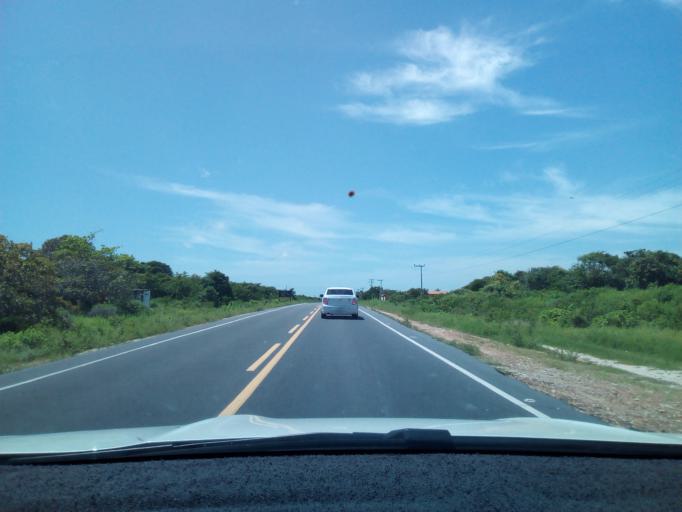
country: BR
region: Ceara
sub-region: Aracati
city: Aracati
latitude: -4.3772
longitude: -37.9178
